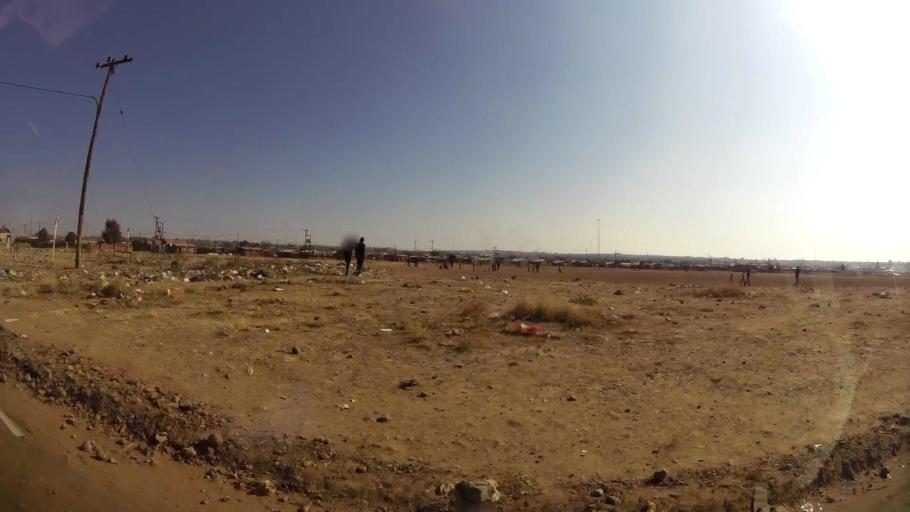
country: ZA
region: Orange Free State
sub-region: Mangaung Metropolitan Municipality
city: Bloemfontein
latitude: -29.1993
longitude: 26.2546
